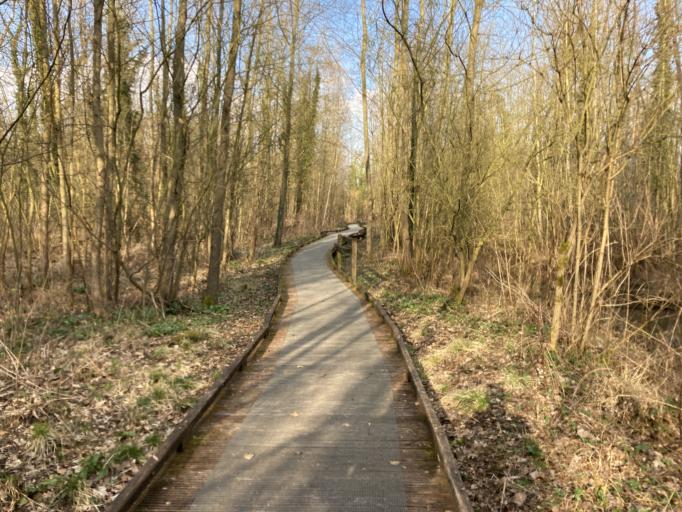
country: FR
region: Nord-Pas-de-Calais
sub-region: Departement du Pas-de-Calais
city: Annequin
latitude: 50.5222
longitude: 2.7071
